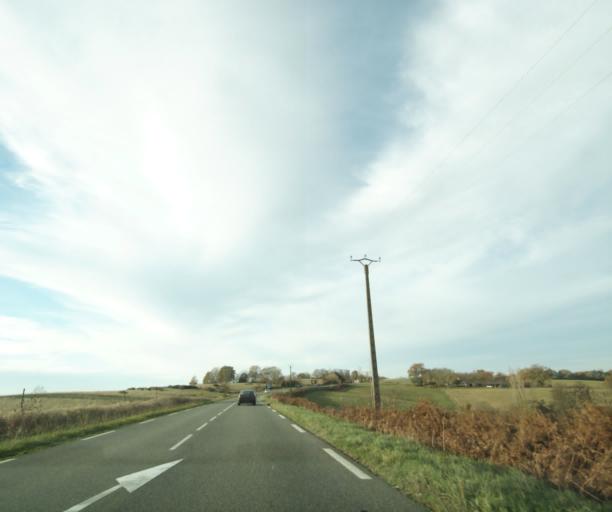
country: FR
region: Midi-Pyrenees
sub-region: Departement du Gers
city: Eauze
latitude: 43.7867
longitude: 0.1082
